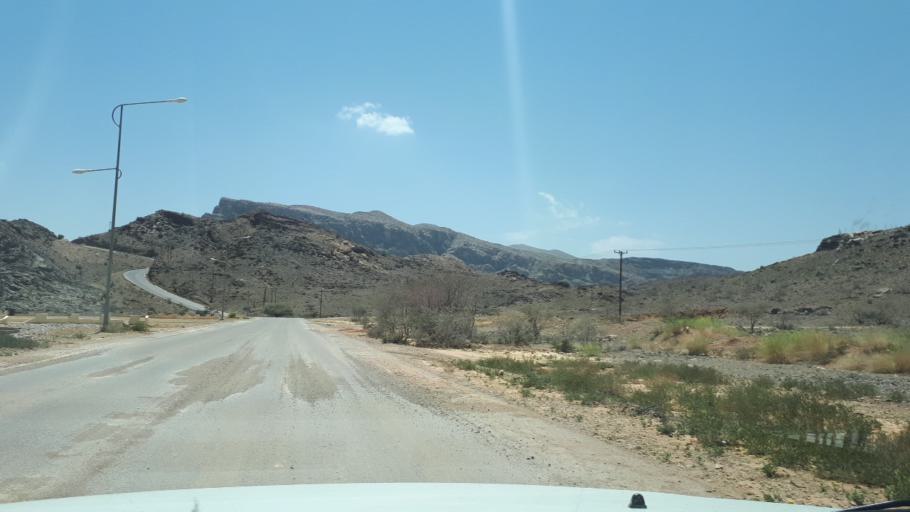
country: OM
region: Muhafazat ad Dakhiliyah
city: Bahla'
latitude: 23.2383
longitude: 57.1497
